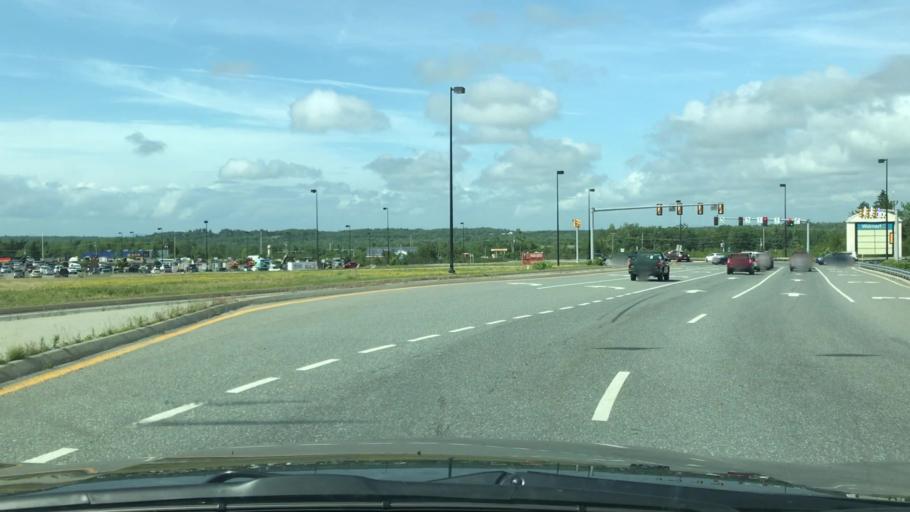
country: US
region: Maine
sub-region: Hancock County
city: Ellsworth
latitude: 44.5257
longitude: -68.3975
